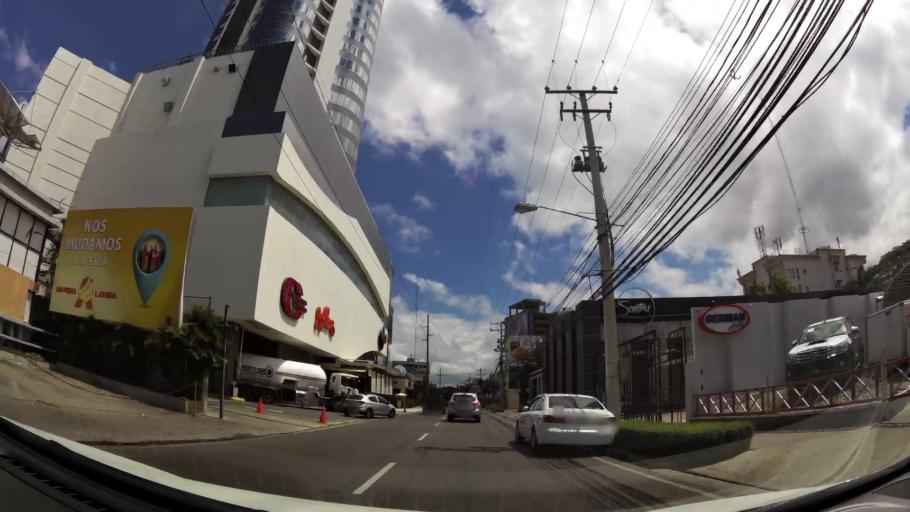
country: DO
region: Nacional
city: La Julia
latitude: 18.4756
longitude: -69.9279
